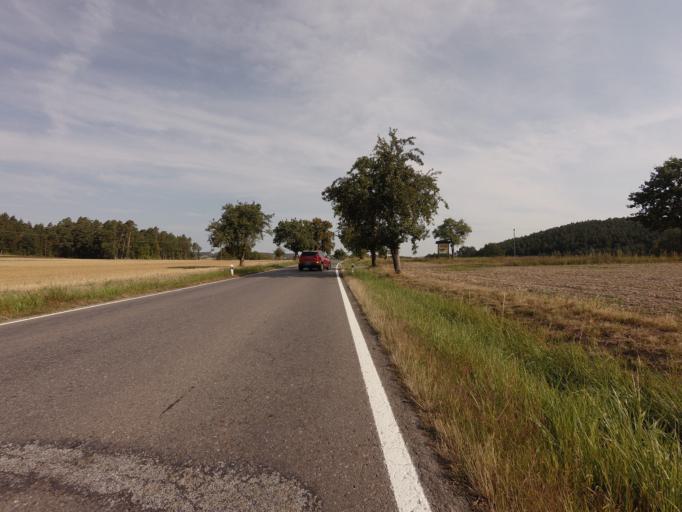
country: CZ
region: Jihocesky
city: Milevsko
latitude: 49.4666
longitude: 14.3617
